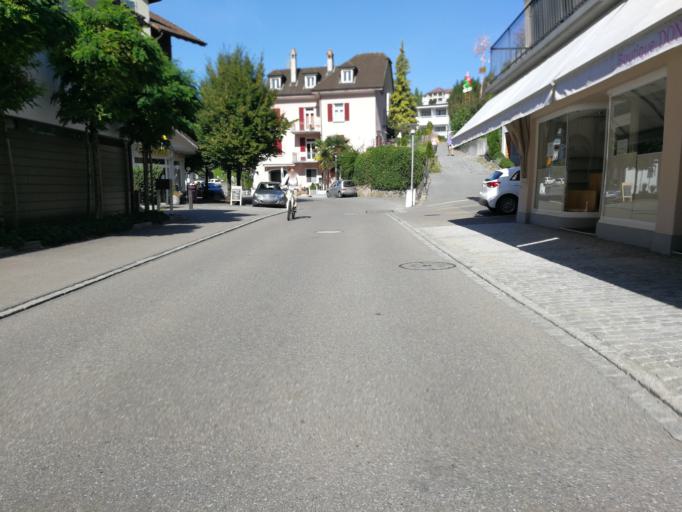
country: CH
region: Lucerne
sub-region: Lucerne-Land District
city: Weggis
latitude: 47.0315
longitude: 8.4263
